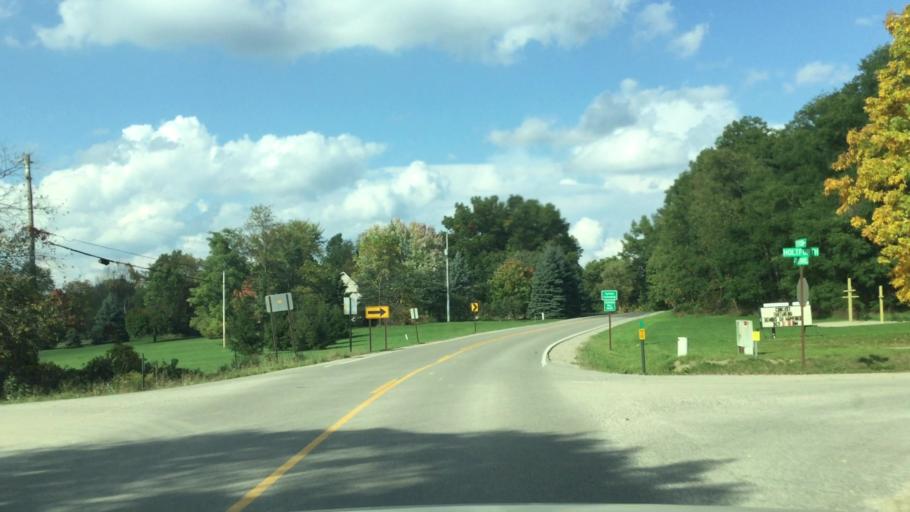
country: US
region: Michigan
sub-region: Genesee County
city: Fenton
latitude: 42.6948
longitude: -83.7032
